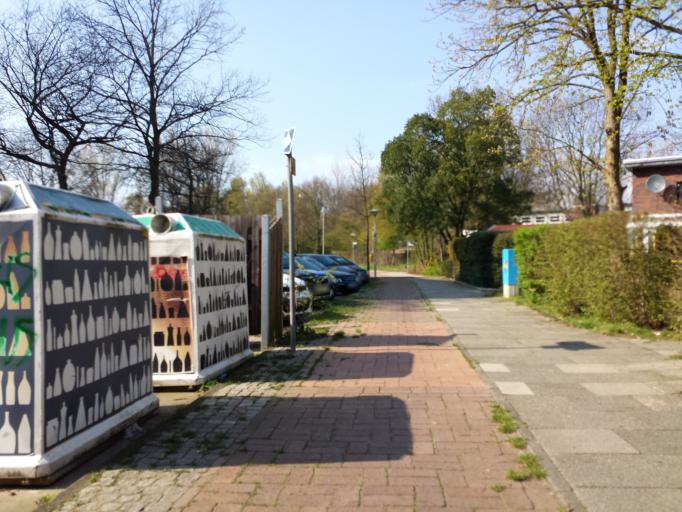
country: DE
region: Lower Saxony
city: Lilienthal
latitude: 53.0855
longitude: 8.8982
